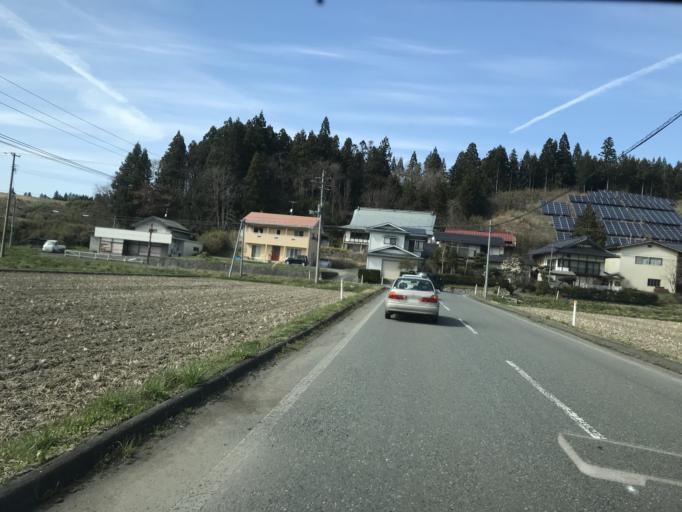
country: JP
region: Iwate
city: Ichinoseki
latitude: 38.9004
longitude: 141.3863
